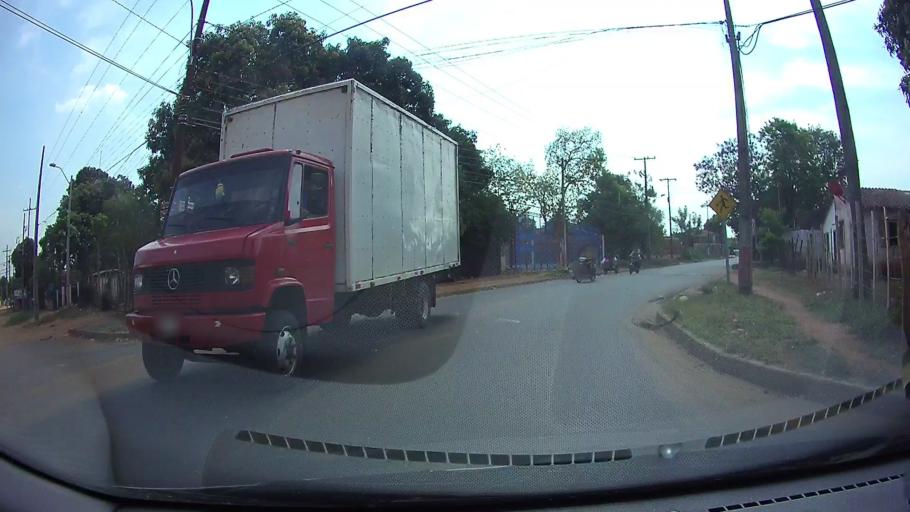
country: PY
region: Central
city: San Lorenzo
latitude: -25.3275
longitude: -57.4993
